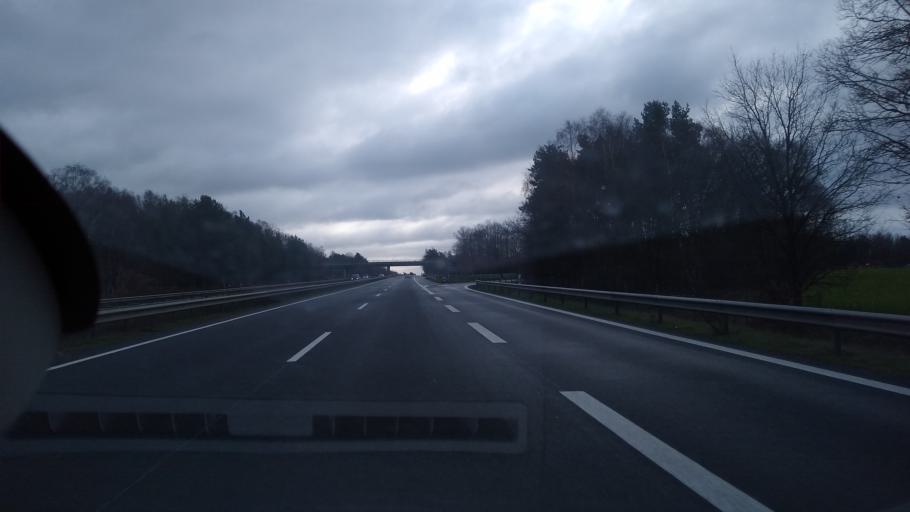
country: DE
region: Lower Saxony
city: Verden
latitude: 52.9615
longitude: 9.2426
